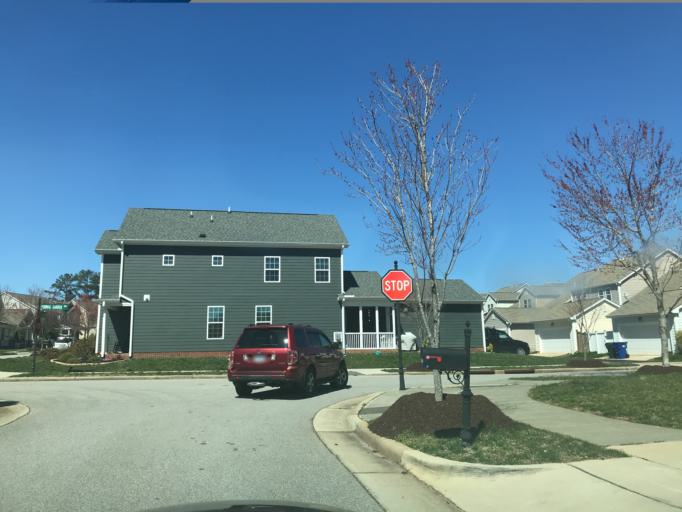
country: US
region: North Carolina
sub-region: Wake County
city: Raleigh
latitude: 35.7363
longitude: -78.6605
